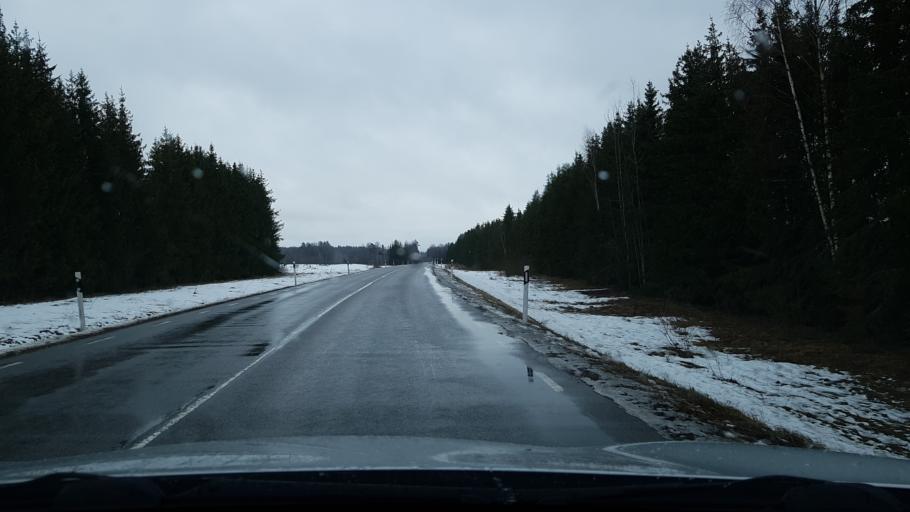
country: LV
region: Apes Novads
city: Ape
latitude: 57.5916
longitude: 26.6372
